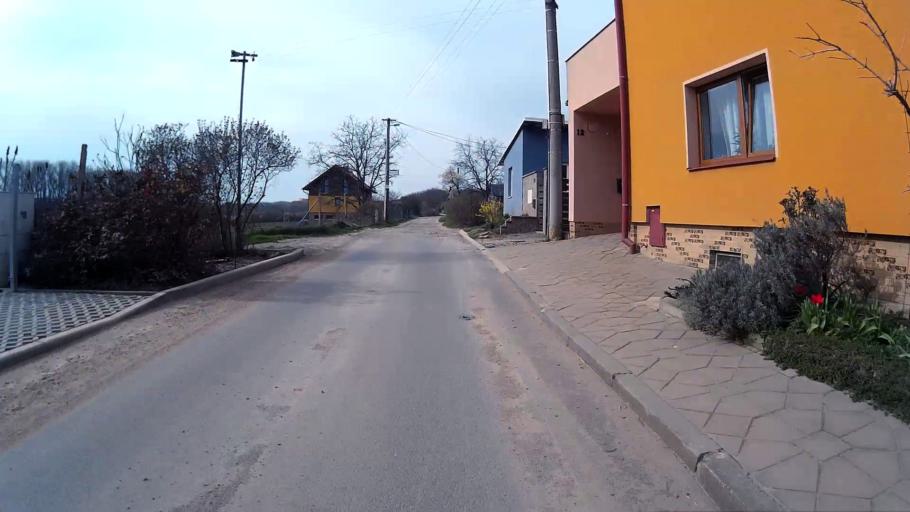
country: CZ
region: South Moravian
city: Dolni Kounice
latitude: 49.0567
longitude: 16.4871
